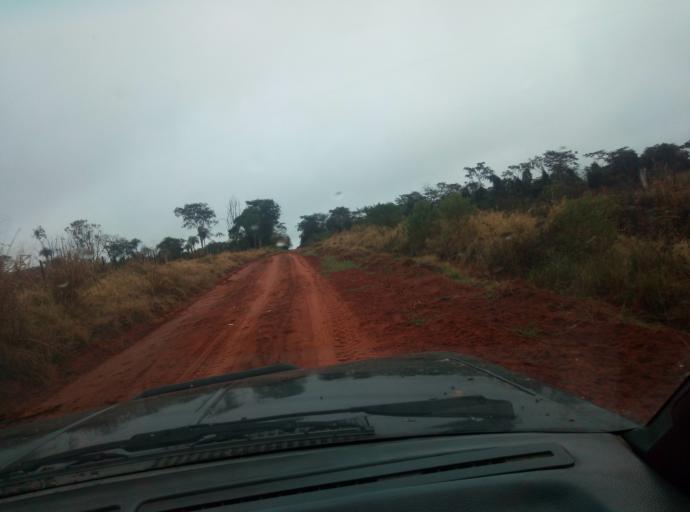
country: PY
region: Caaguazu
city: Carayao
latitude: -25.1924
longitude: -56.3375
